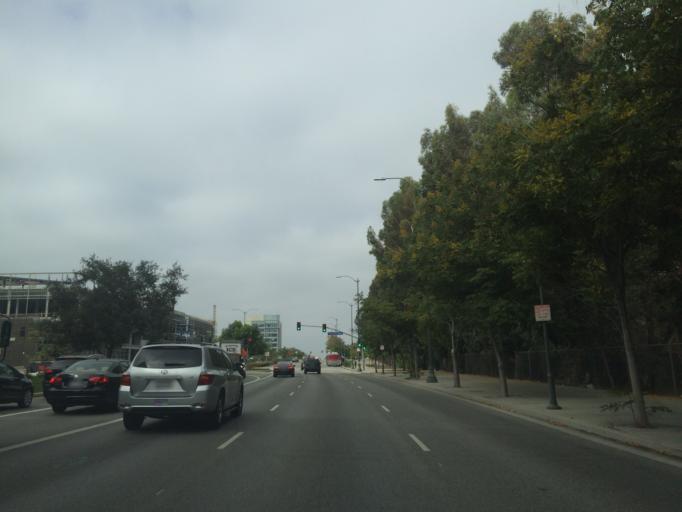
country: US
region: California
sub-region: Los Angeles County
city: Century City
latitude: 34.0621
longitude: -118.4177
